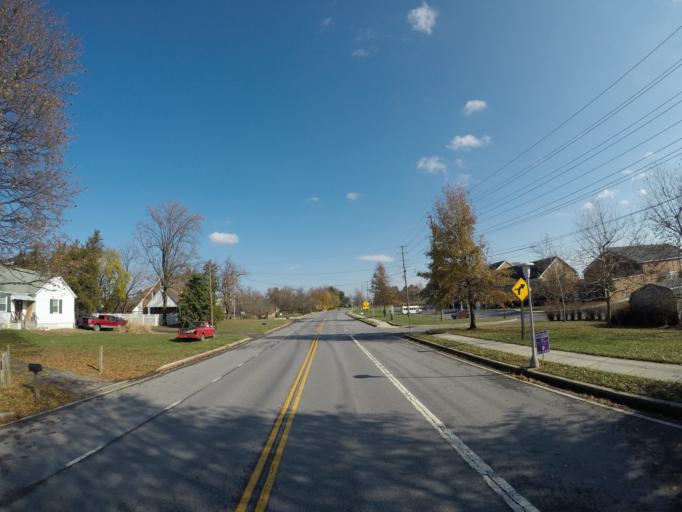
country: US
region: Maryland
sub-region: Frederick County
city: Ballenger Creek
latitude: 39.4024
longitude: -77.4449
